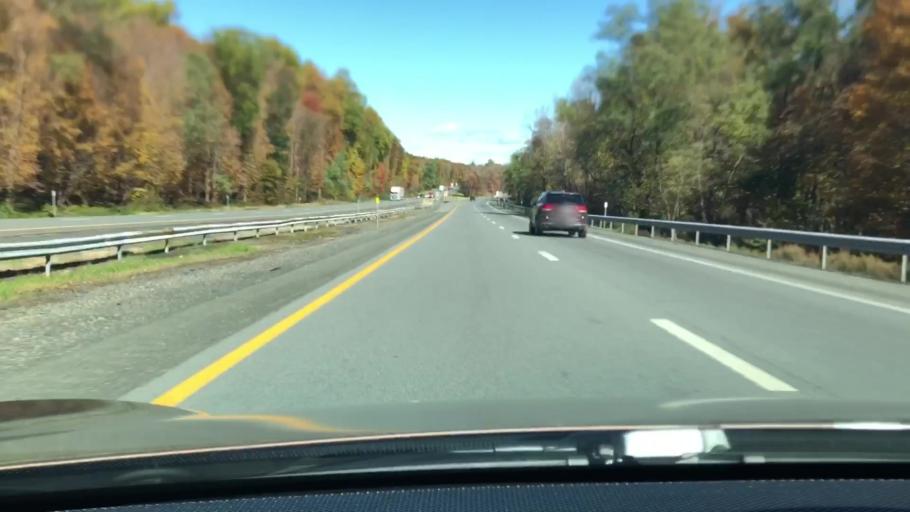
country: US
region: New York
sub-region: Orange County
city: Woodbury
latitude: 41.3897
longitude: -74.0966
